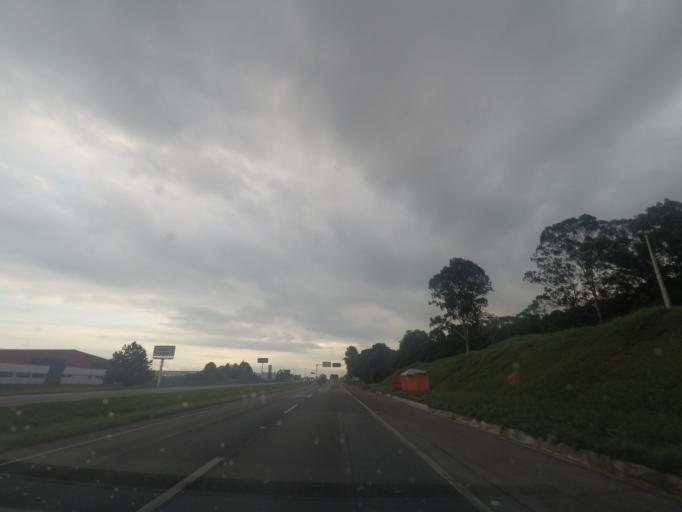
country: BR
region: Parana
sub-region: Sao Jose Dos Pinhais
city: Sao Jose dos Pinhais
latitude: -25.5704
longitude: -49.1905
